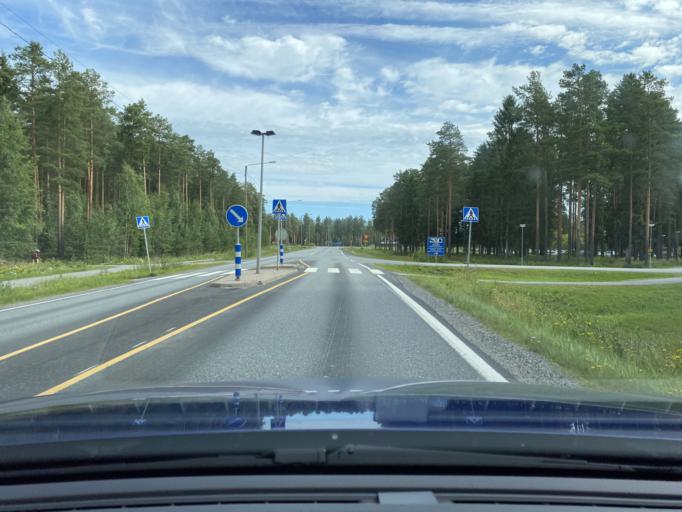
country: FI
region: Southern Ostrobothnia
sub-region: Seinaejoki
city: Ylihaermae
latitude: 63.1423
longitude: 22.8215
